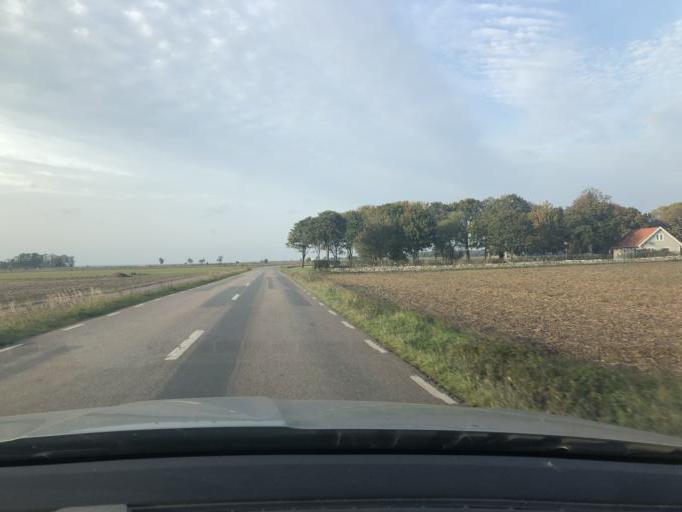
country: SE
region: Kalmar
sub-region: Morbylanga Kommun
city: Moerbylanga
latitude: 56.2958
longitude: 16.4098
